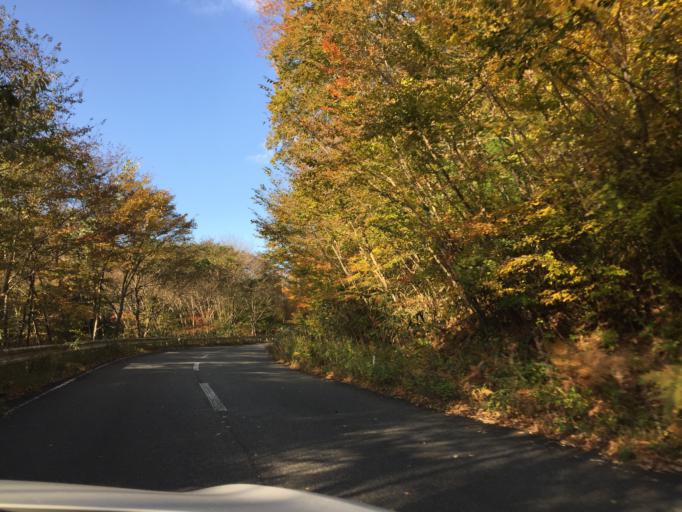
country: JP
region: Fukushima
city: Iwaki
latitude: 37.2407
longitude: 140.7623
